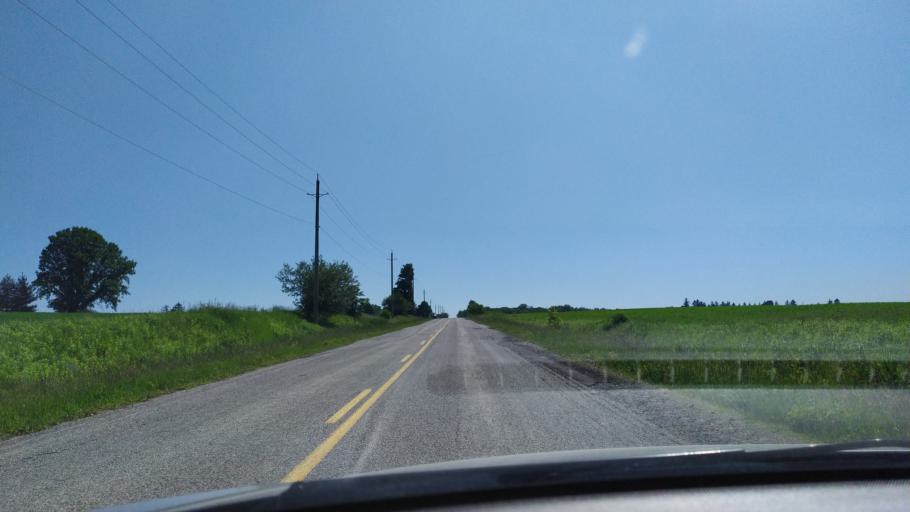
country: CA
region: Ontario
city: Waterloo
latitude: 43.4564
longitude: -80.7351
